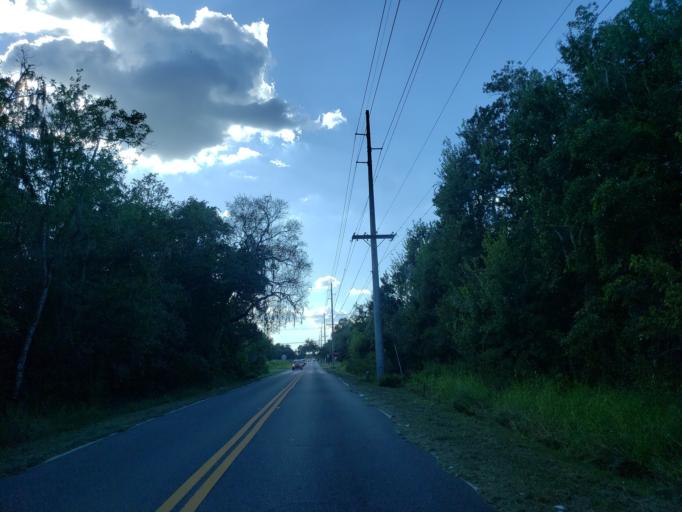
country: US
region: Florida
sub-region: Hillsborough County
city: Dover
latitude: 27.9670
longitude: -82.2185
